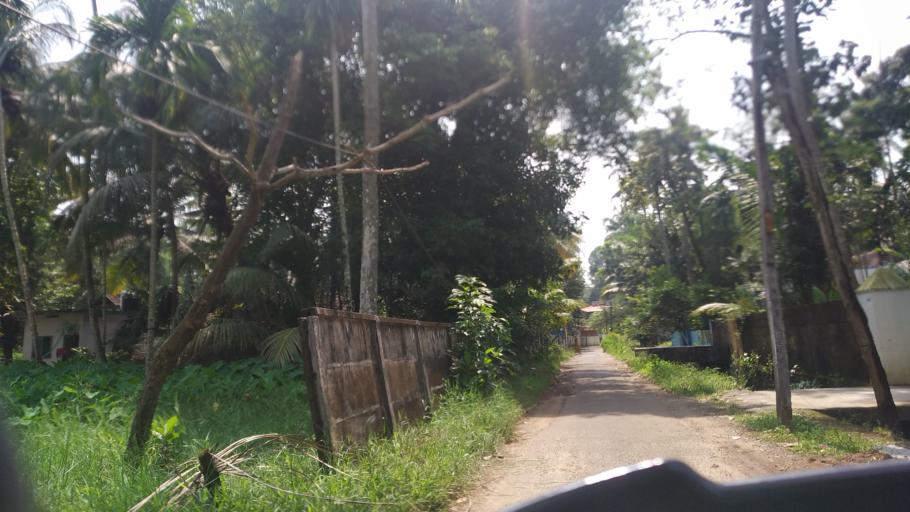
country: IN
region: Kerala
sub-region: Ernakulam
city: Elur
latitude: 10.0598
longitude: 76.2159
